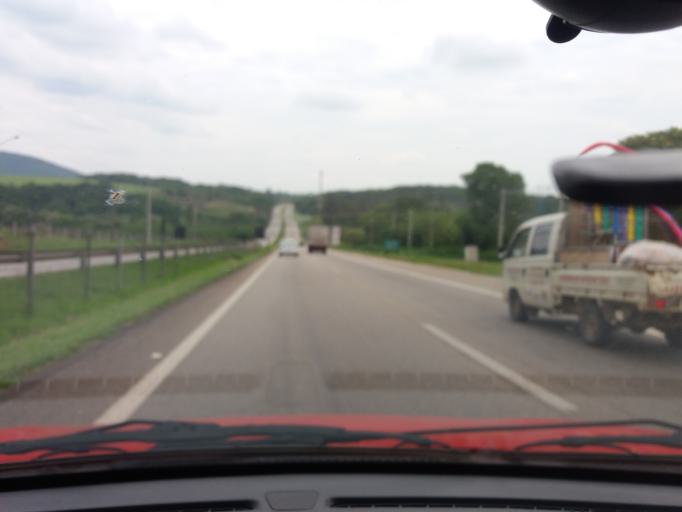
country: BR
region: Sao Paulo
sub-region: Itupeva
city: Itupeva
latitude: -23.1922
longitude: -46.9907
